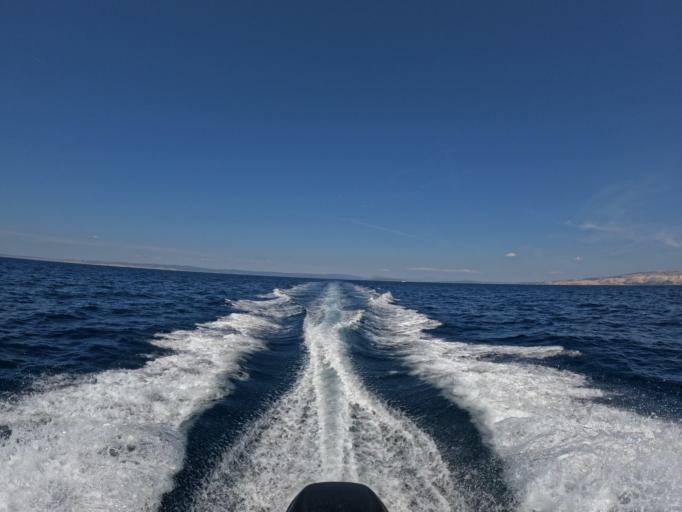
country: HR
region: Primorsko-Goranska
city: Lopar
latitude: 44.8653
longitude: 14.6804
